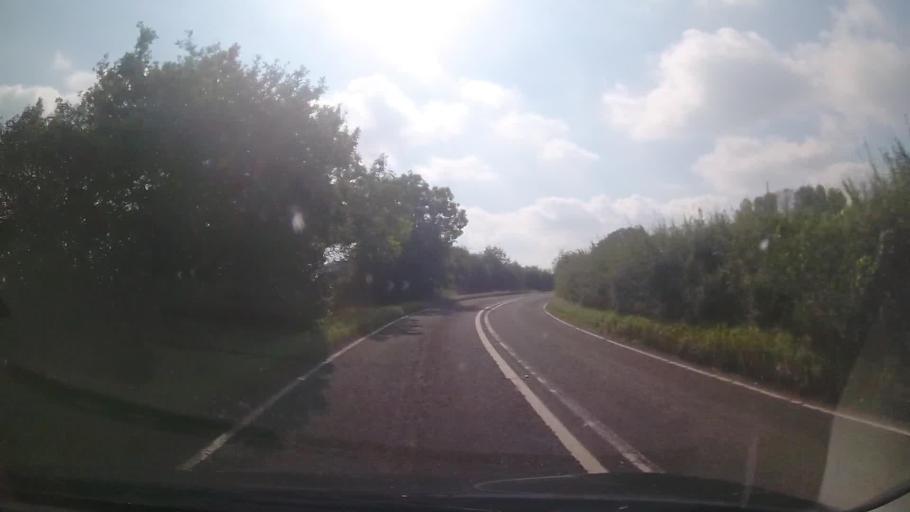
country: GB
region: England
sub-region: Cheshire West and Chester
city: Beeston
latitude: 53.0910
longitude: -2.6631
